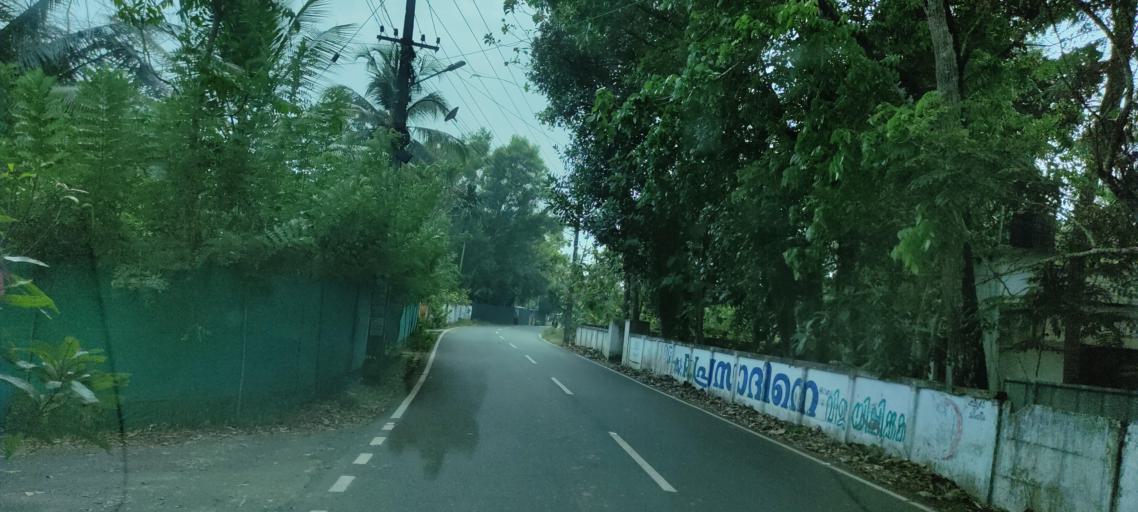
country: IN
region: Kerala
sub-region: Alappuzha
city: Shertallai
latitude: 9.5987
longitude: 76.3410
